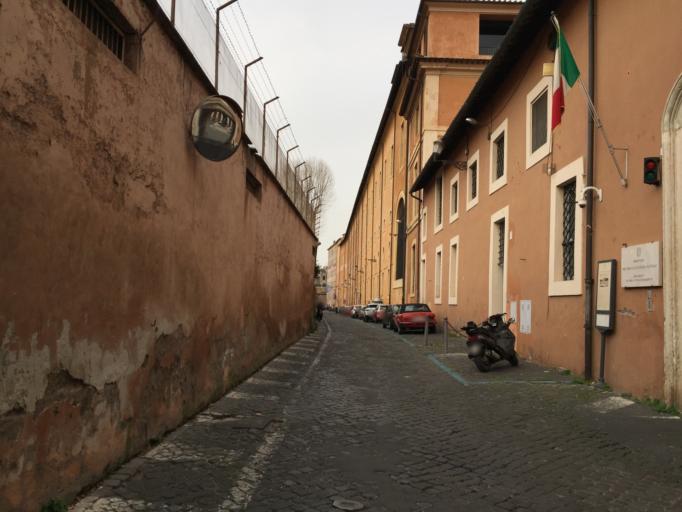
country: VA
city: Vatican City
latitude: 41.8850
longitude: 12.4749
